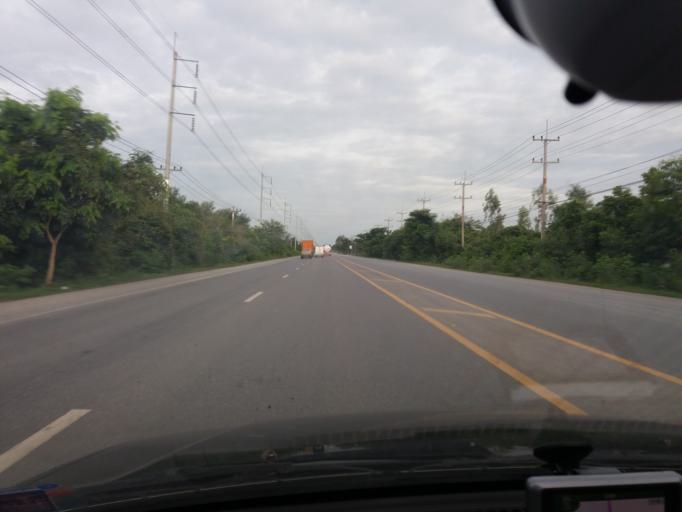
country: TH
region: Suphan Buri
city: U Thong
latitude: 14.3375
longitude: 99.8368
